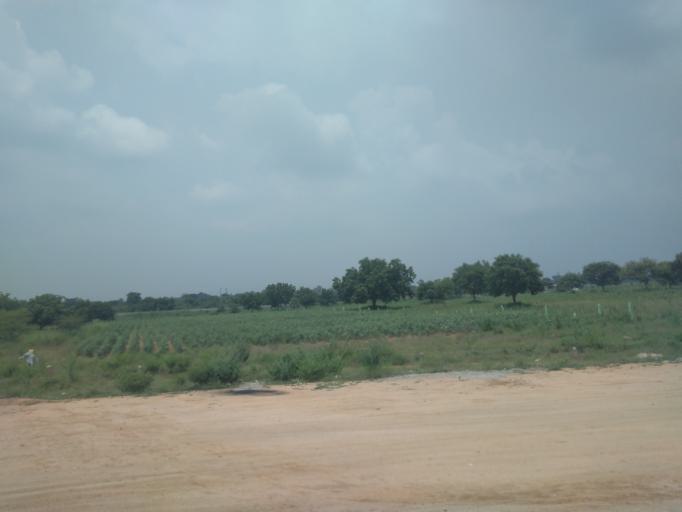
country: IN
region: Telangana
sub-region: Warangal
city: Jangaon
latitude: 17.6612
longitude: 79.0799
